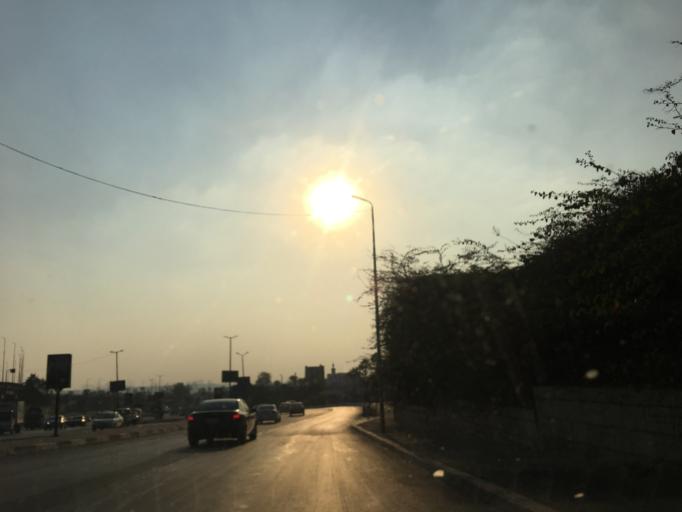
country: EG
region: Muhafazat al Qahirah
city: Cairo
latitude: 30.0275
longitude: 31.2635
